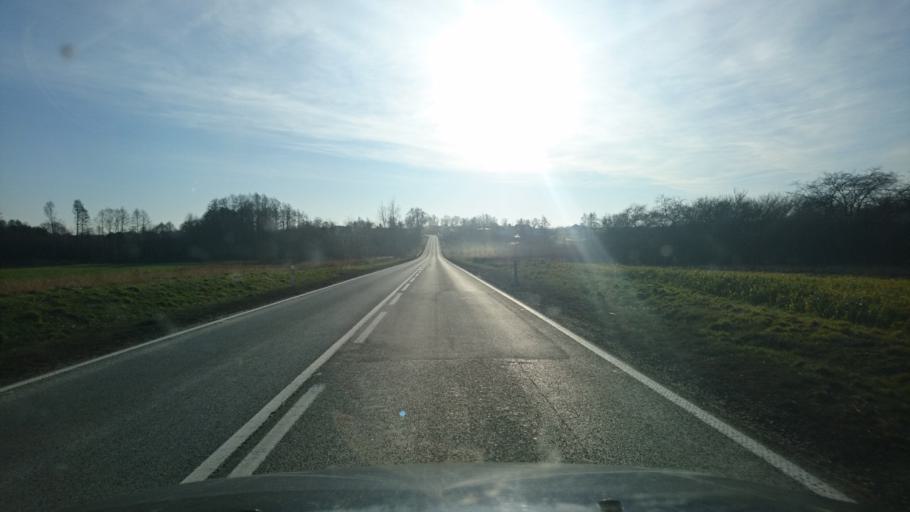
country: PL
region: Opole Voivodeship
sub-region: Powiat oleski
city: Dalachow
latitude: 51.0482
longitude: 18.5975
